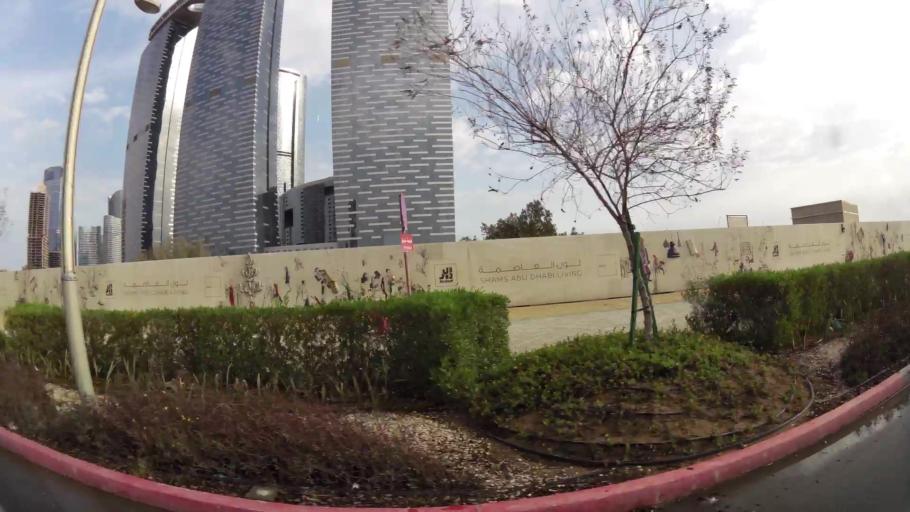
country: AE
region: Abu Dhabi
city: Abu Dhabi
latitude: 24.4915
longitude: 54.4085
